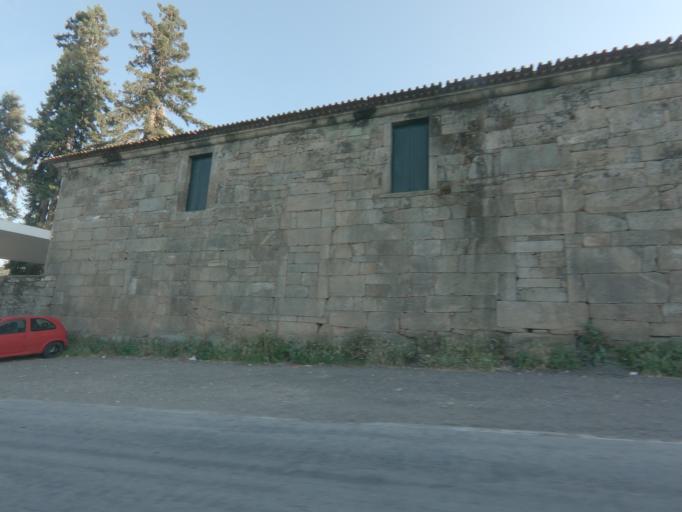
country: PT
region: Vila Real
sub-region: Vila Real
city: Vila Real
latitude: 41.2973
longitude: -7.7120
